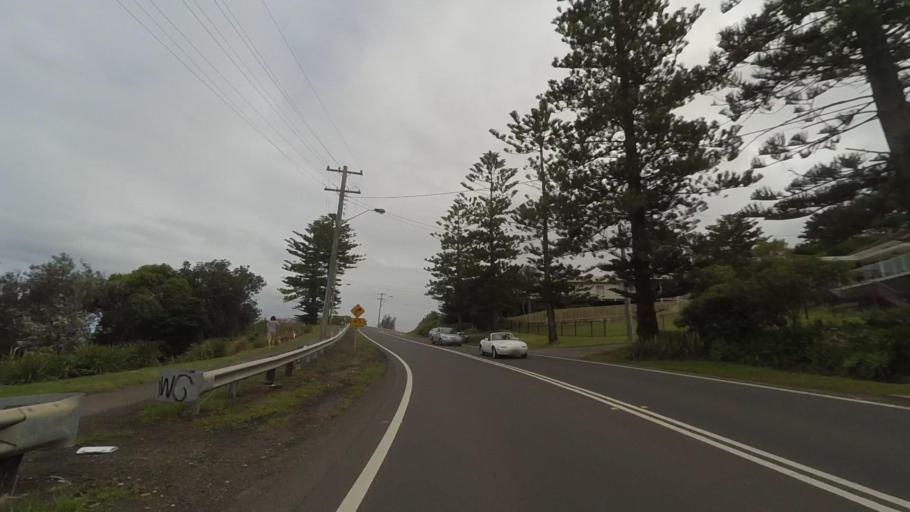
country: AU
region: New South Wales
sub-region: Wollongong
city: Bulli
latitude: -34.2978
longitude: 150.9406
